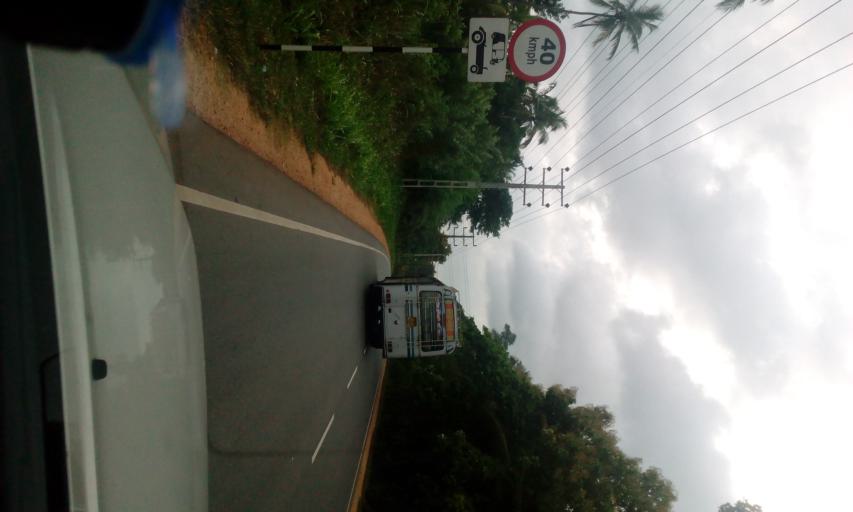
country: LK
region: Western
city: Minuwangoda
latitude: 7.3161
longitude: 79.9593
